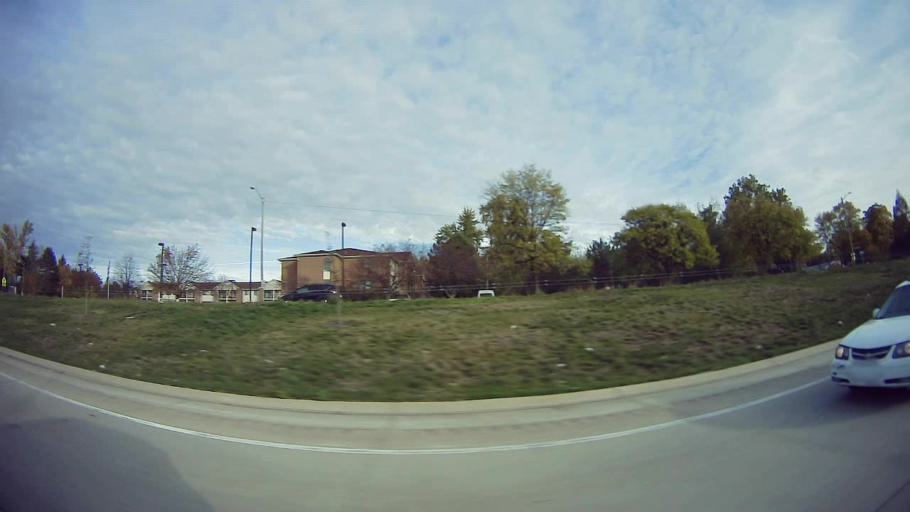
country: US
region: Michigan
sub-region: Wayne County
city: Redford
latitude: 42.3852
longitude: -83.3045
